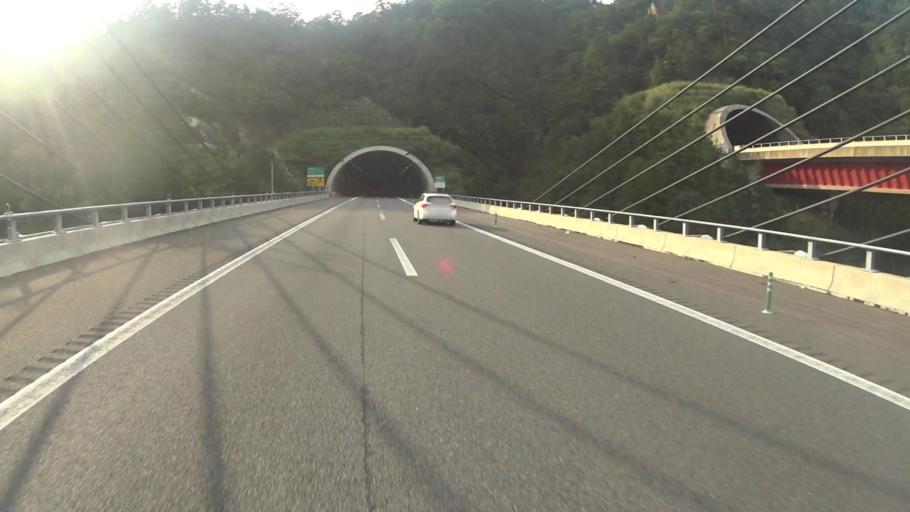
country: JP
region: Shiga Prefecture
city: Kusatsu
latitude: 34.9412
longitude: 136.0319
